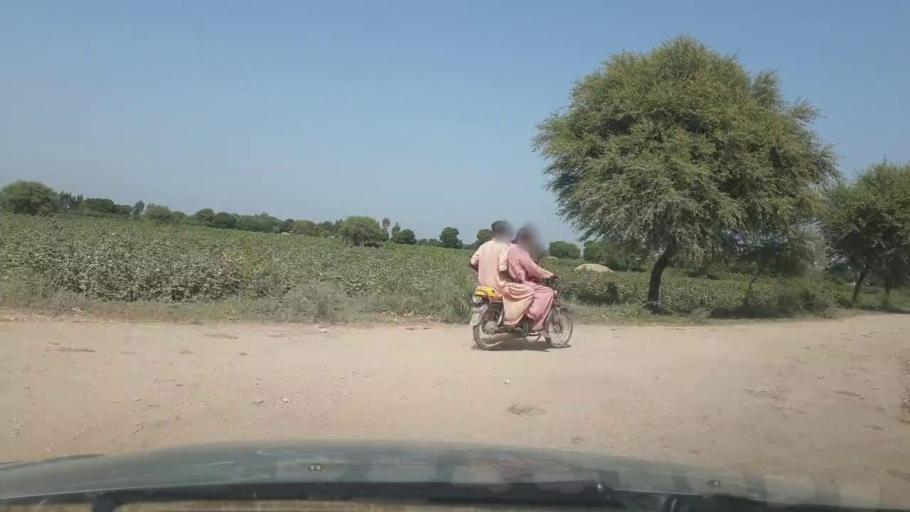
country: PK
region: Sindh
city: Tando Ghulam Ali
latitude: 25.1792
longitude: 68.8737
